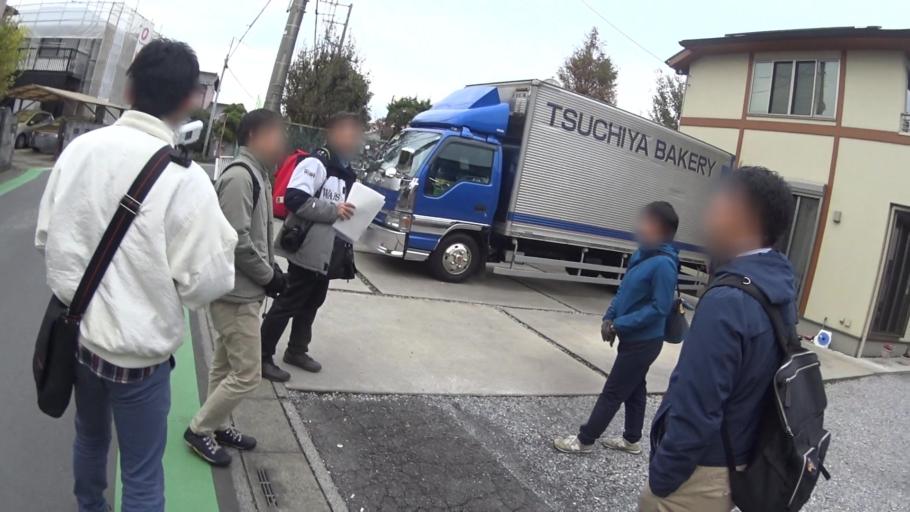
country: JP
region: Saitama
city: Yashio-shi
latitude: 35.8332
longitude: 139.8468
